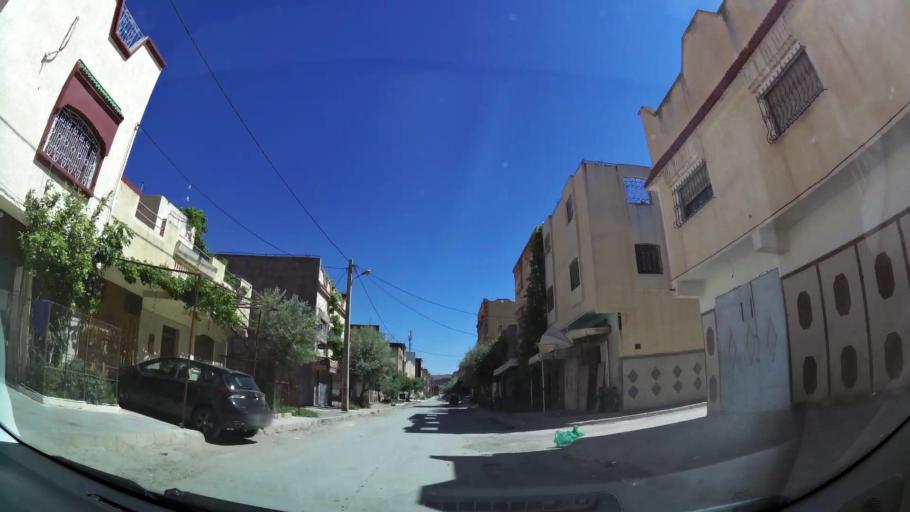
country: MA
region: Oriental
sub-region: Oujda-Angad
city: Oujda
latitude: 34.6648
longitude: -1.8795
